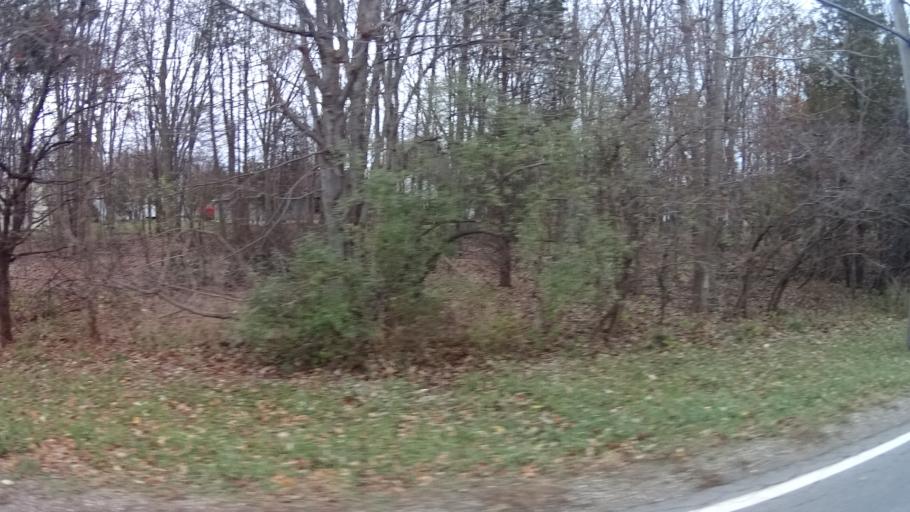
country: US
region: Ohio
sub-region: Lorain County
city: Avon Lake
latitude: 41.4909
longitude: -81.9885
